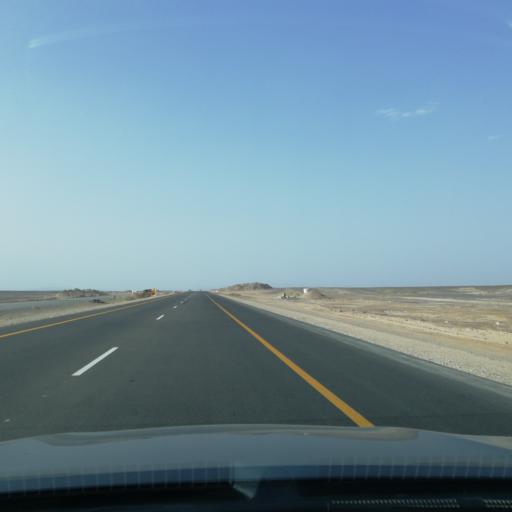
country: OM
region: Muhafazat ad Dakhiliyah
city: Adam
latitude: 22.1706
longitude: 57.5216
